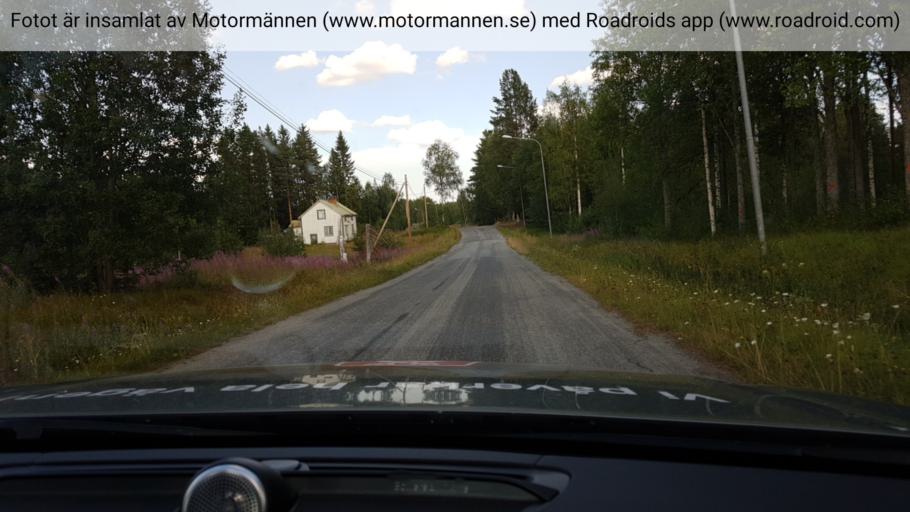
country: SE
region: Vaesterbotten
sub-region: Dorotea Kommun
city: Dorotea
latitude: 63.9130
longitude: 16.3085
